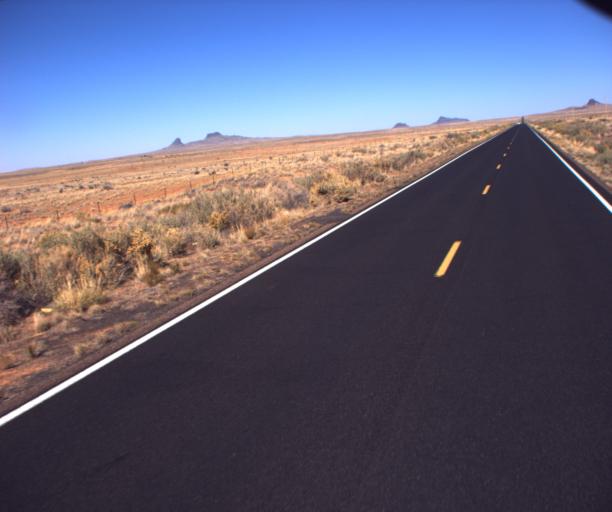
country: US
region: Arizona
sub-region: Navajo County
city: Dilkon
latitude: 35.3372
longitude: -110.4237
